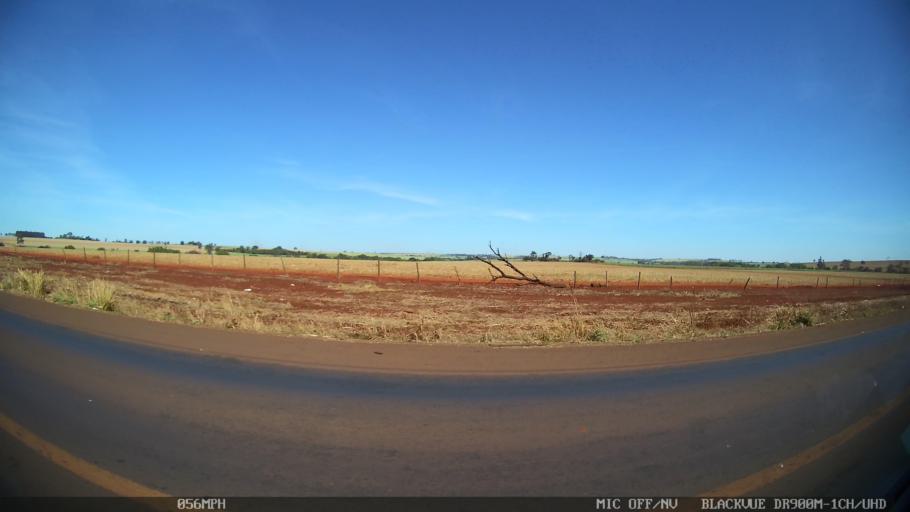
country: BR
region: Sao Paulo
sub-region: Sao Joaquim Da Barra
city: Sao Joaquim da Barra
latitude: -20.5150
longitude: -47.8887
